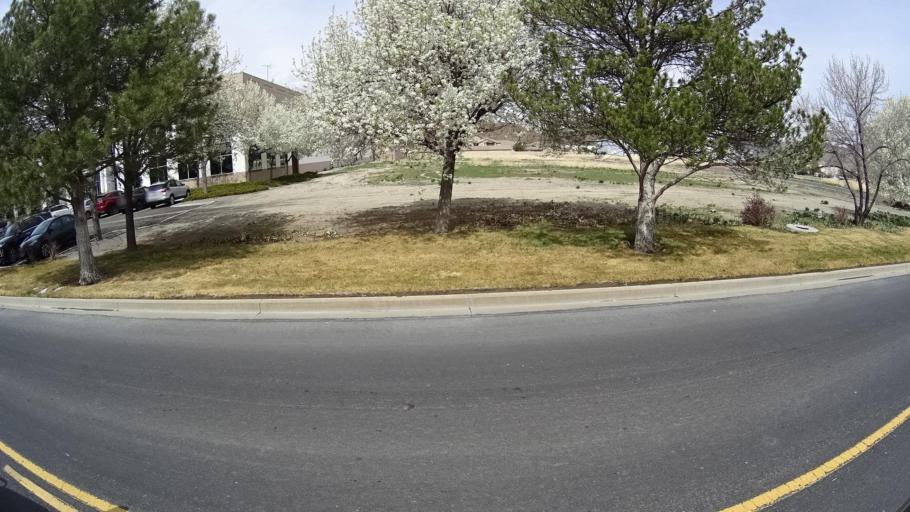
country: US
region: Nevada
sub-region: Washoe County
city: Sparks
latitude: 39.4479
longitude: -119.7550
